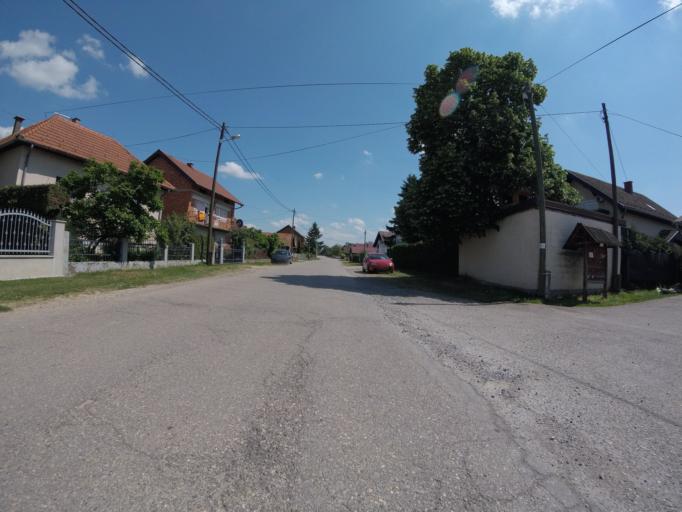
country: HR
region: Zagrebacka
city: Mraclin
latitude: 45.6748
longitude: 16.0694
